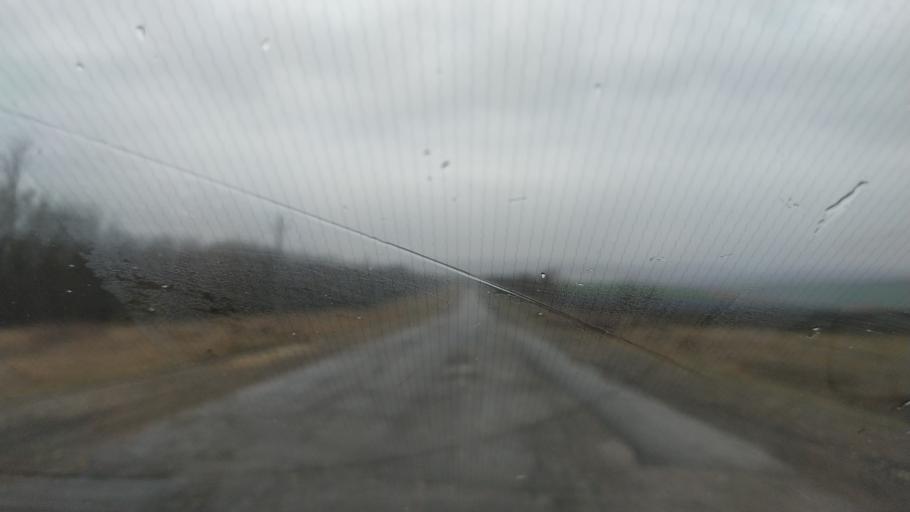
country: MD
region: Cantemir
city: Visniovca
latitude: 46.3221
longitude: 28.5345
